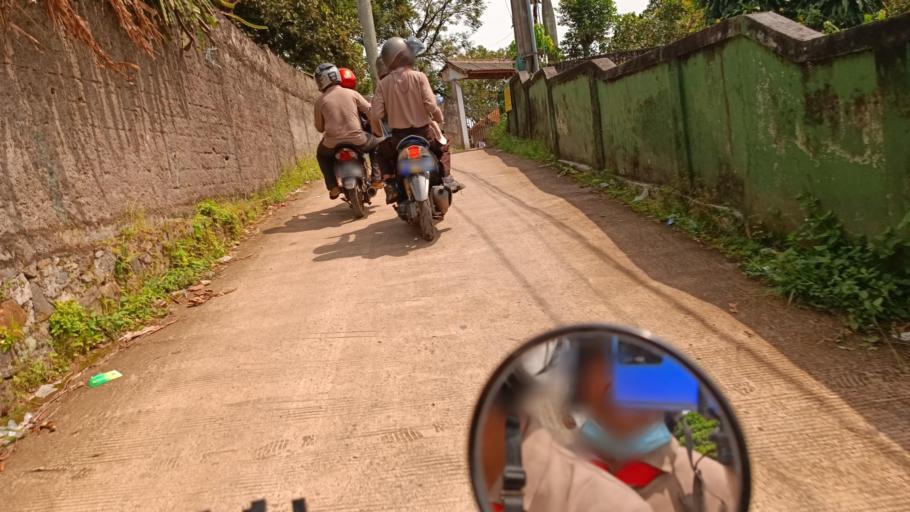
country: ID
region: West Java
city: Caringin
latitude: -6.6540
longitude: 106.8912
